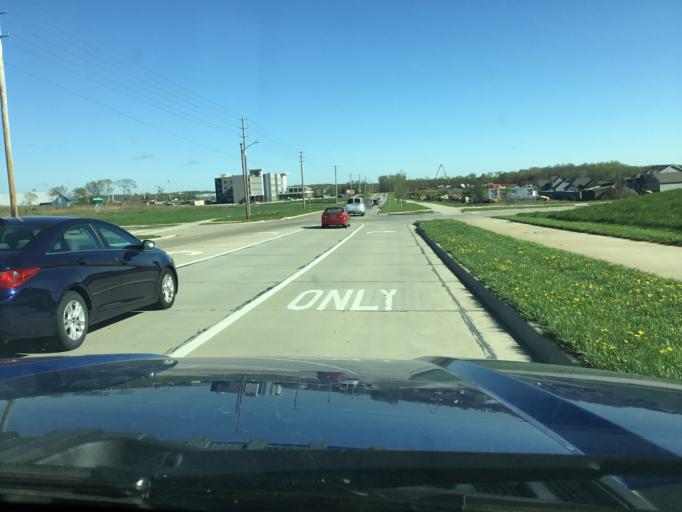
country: US
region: Kansas
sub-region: Douglas County
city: Lawrence
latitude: 38.9750
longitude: -95.3257
